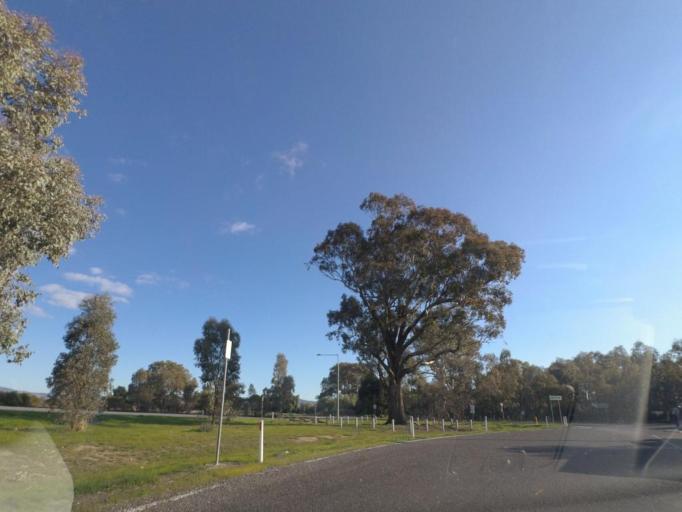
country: AU
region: Victoria
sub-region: Benalla
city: Benalla
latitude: -36.6962
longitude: 145.6592
